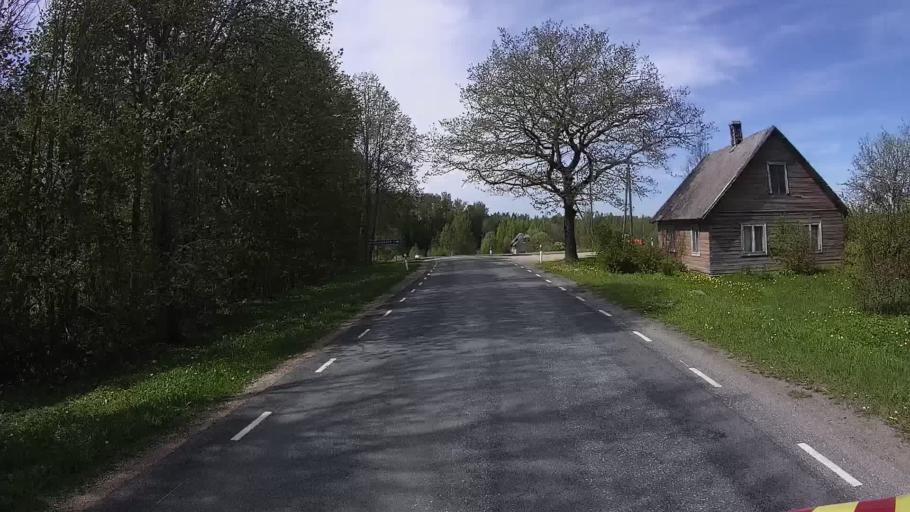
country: EE
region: Valgamaa
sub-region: Valga linn
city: Valga
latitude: 57.6523
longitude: 26.3010
